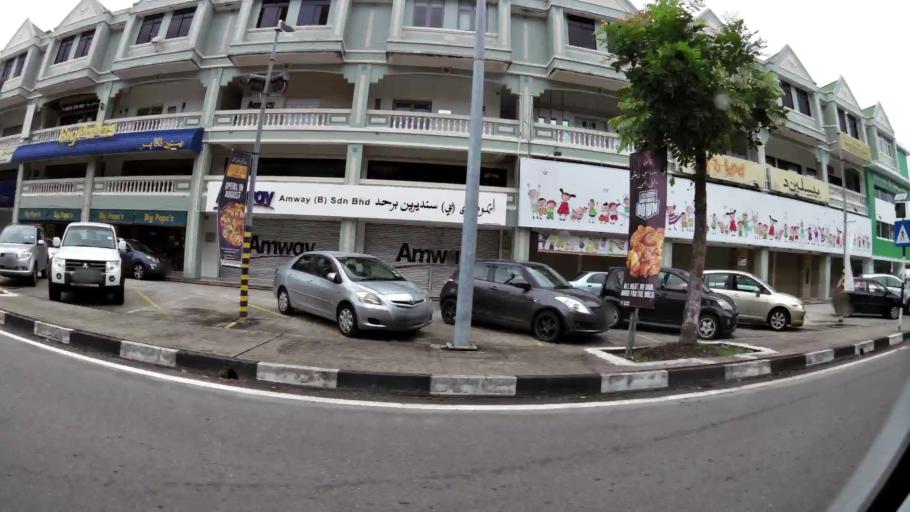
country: BN
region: Brunei and Muara
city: Bandar Seri Begawan
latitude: 4.9033
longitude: 114.9276
